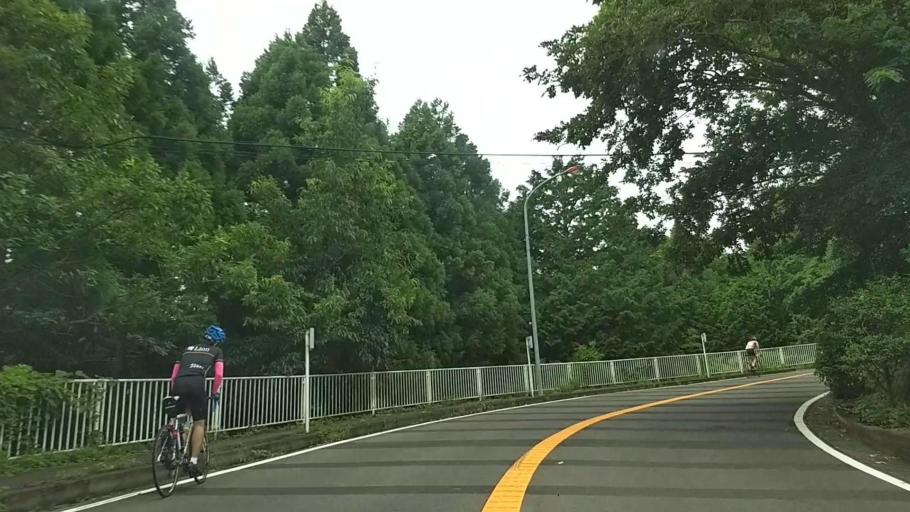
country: JP
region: Shizuoka
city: Gotemba
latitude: 35.3233
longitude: 139.0499
